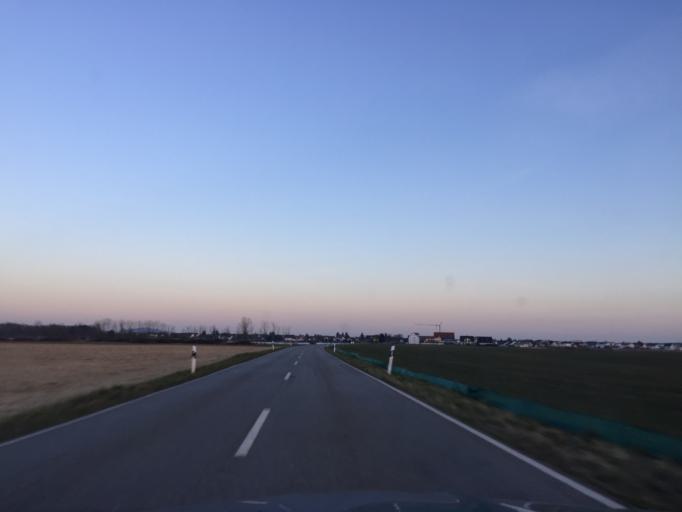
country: DE
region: Baden-Wuerttemberg
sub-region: Karlsruhe Region
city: Reilingen
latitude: 49.2784
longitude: 8.5844
